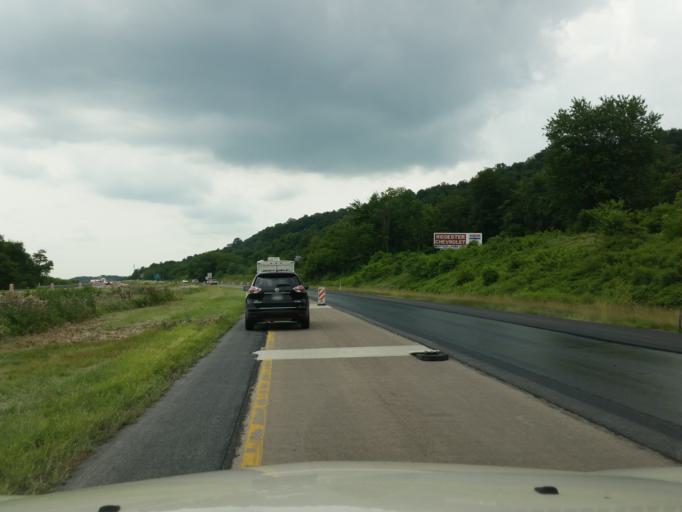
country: US
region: Pennsylvania
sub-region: Perry County
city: Newport
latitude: 40.5712
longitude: -77.2093
